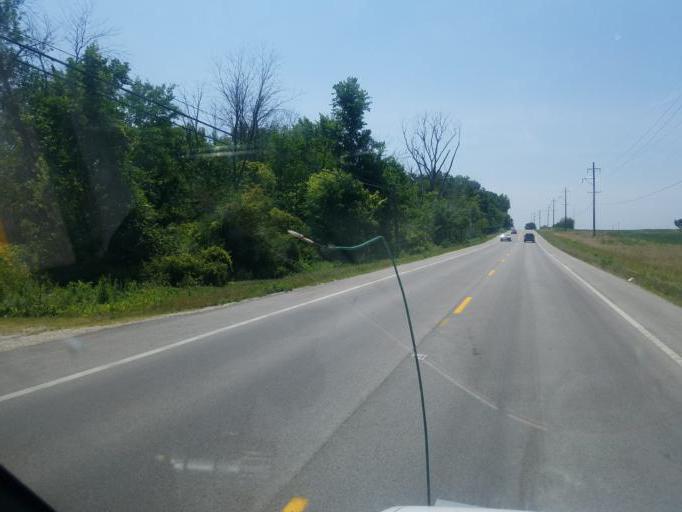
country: US
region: Ohio
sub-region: Mercer County
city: Celina
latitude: 40.5510
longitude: -84.4859
